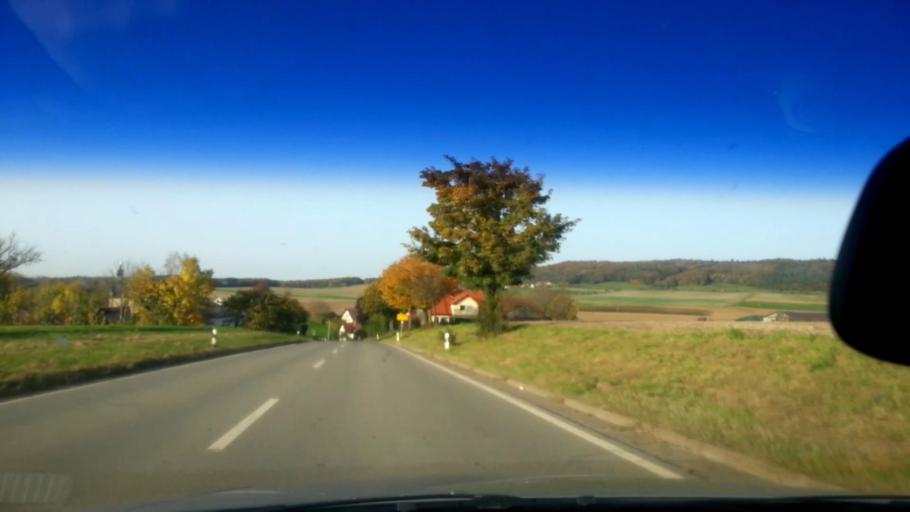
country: DE
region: Bavaria
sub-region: Upper Franconia
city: Schesslitz
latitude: 50.0014
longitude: 11.0189
